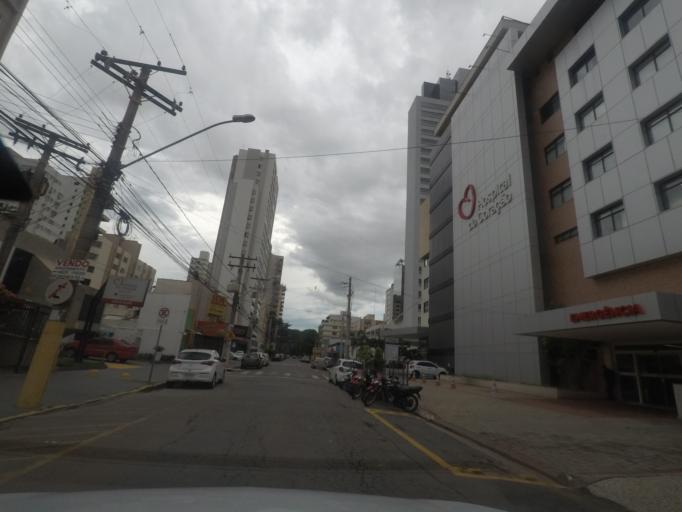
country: BR
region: Goias
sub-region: Goiania
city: Goiania
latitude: -16.6833
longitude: -49.2654
